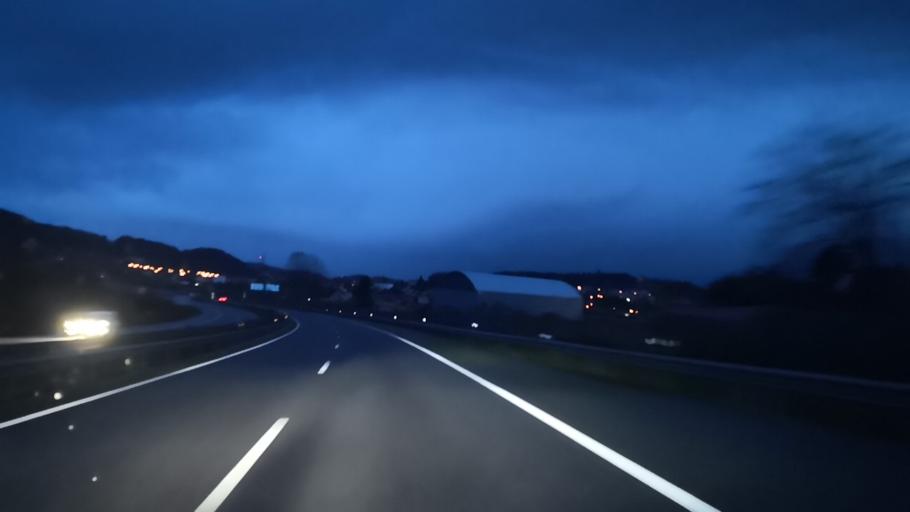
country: PT
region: Braga
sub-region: Braga
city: Oliveira
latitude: 41.4990
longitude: -8.4238
